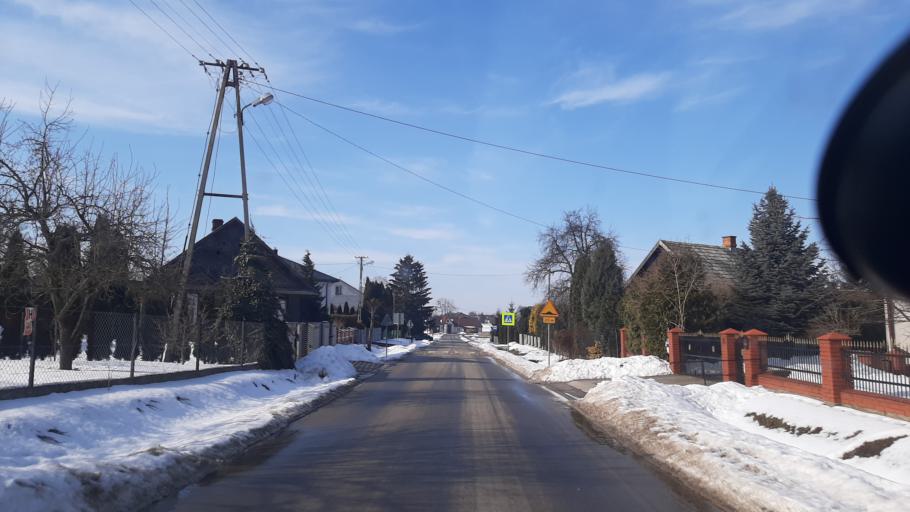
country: PL
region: Lublin Voivodeship
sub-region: Powiat pulawski
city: Baranow
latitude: 51.5377
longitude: 22.1525
